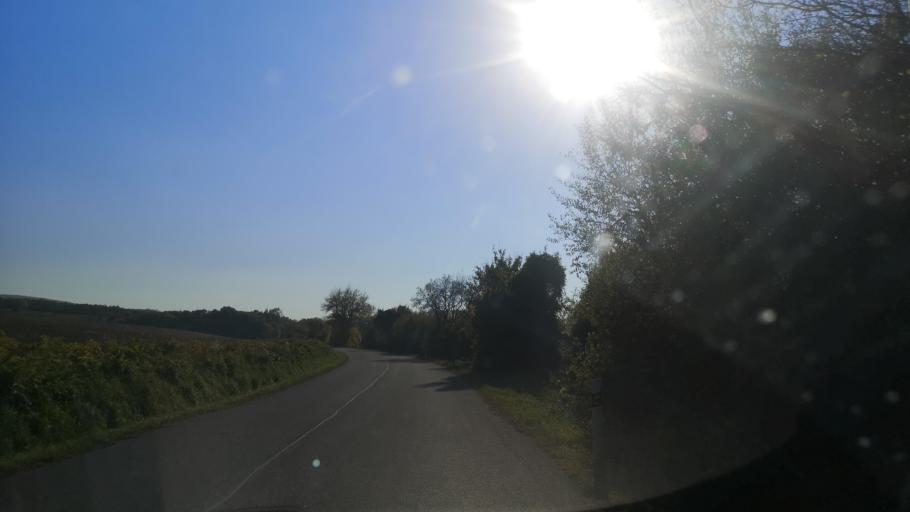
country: SK
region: Nitriansky
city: Zlate Moravce
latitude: 48.4382
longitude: 18.4304
